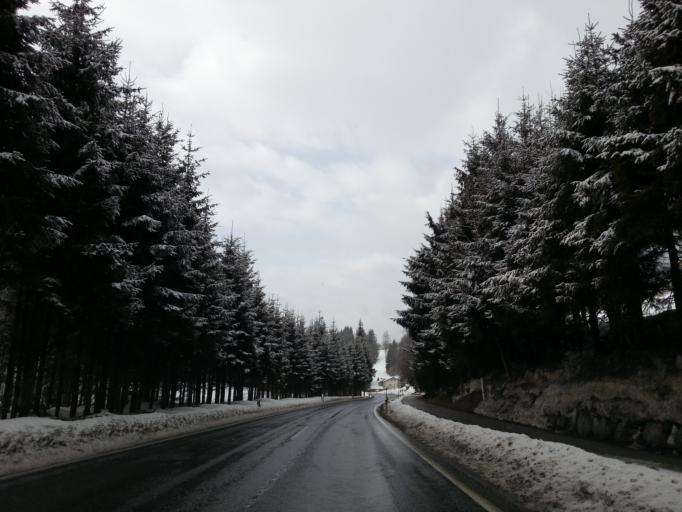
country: AT
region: Salzburg
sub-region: Politischer Bezirk Sankt Johann im Pongau
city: Eben im Pongau
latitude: 47.4506
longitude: 13.3669
